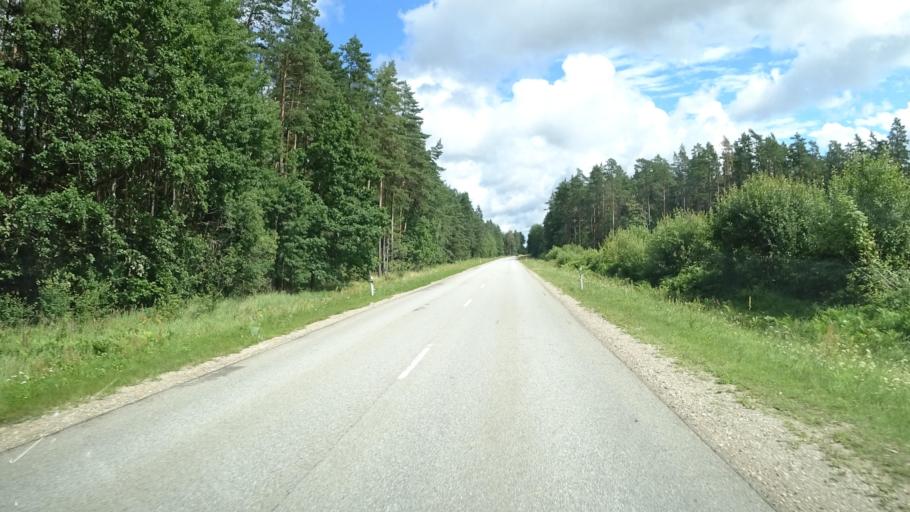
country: LV
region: Pavilostas
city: Pavilosta
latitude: 56.7290
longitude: 21.2039
